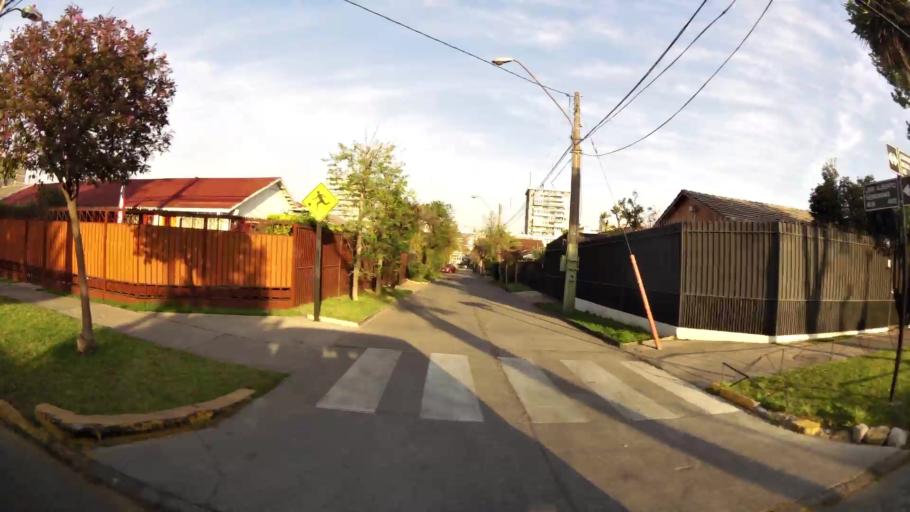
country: CL
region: Santiago Metropolitan
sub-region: Provincia de Santiago
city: Villa Presidente Frei, Nunoa, Santiago, Chile
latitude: -33.4582
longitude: -70.5791
